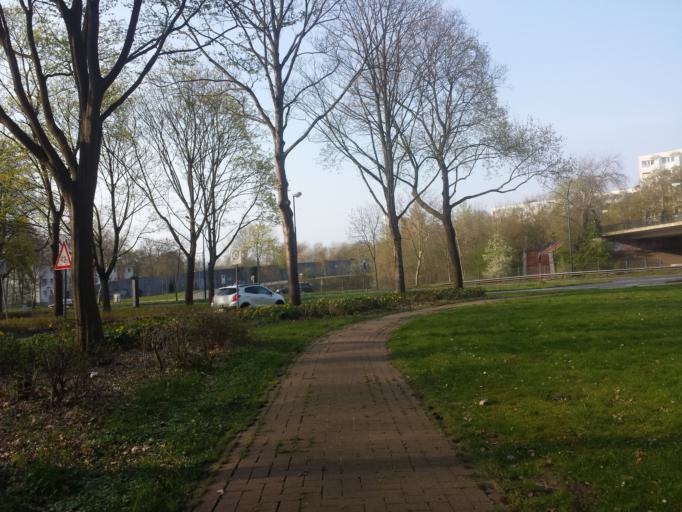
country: DE
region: Lower Saxony
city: Lilienthal
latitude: 53.0819
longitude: 8.8907
